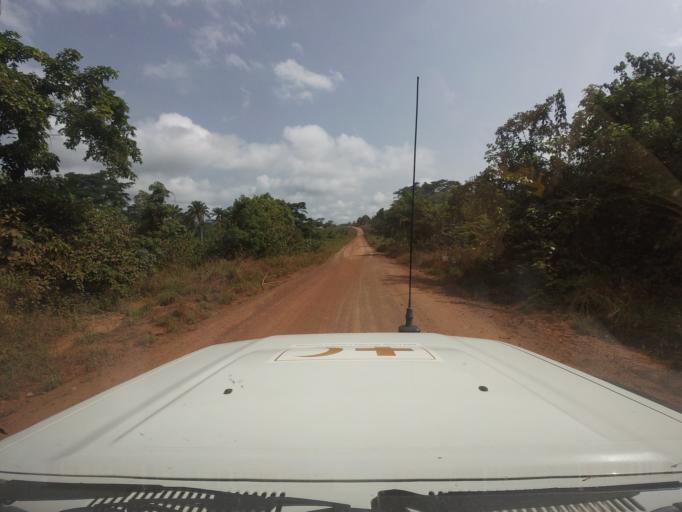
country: LR
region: Bong
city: Gbarnga
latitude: 7.2137
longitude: -9.4397
